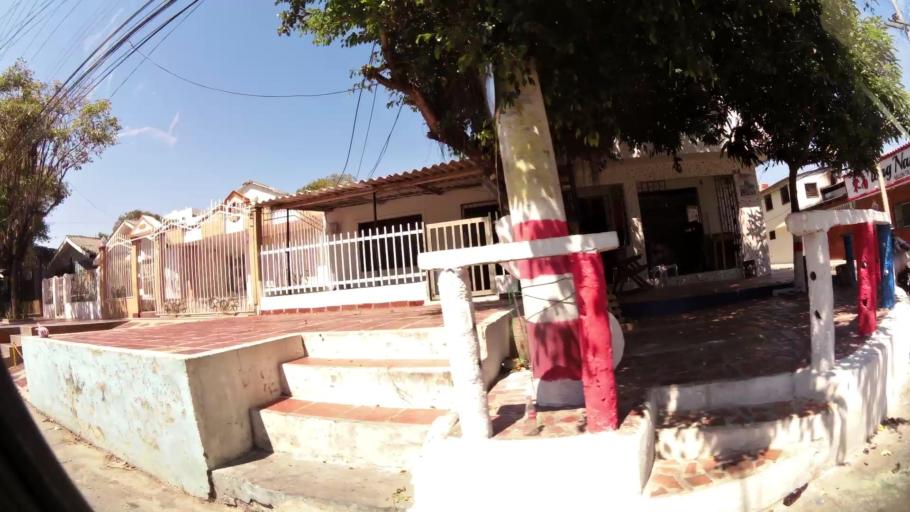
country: CO
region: Atlantico
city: Barranquilla
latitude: 11.0062
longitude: -74.7953
